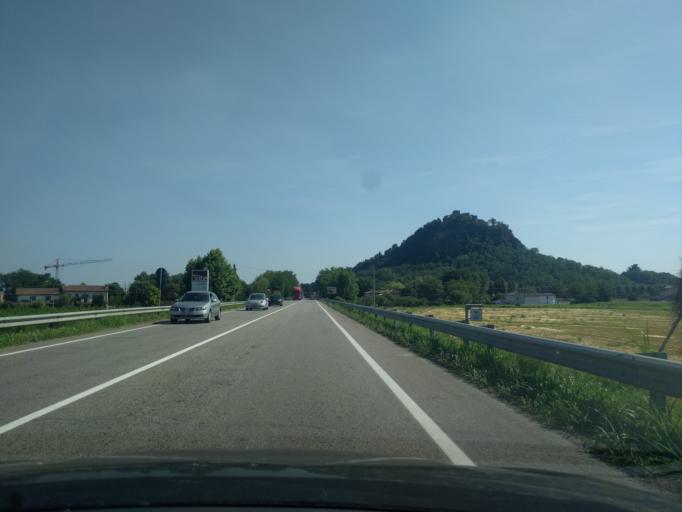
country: IT
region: Veneto
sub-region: Provincia di Padova
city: Monselice
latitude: 45.2509
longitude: 11.7582
